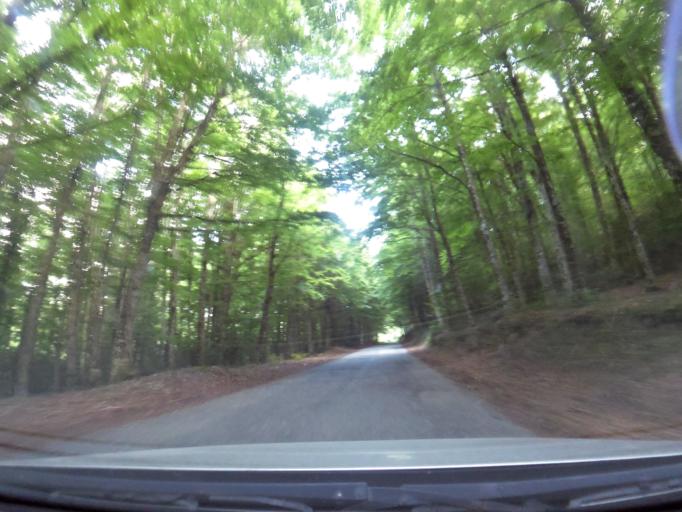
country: IT
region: Calabria
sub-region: Provincia di Vibo-Valentia
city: Nardodipace
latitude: 38.5028
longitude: 16.3819
